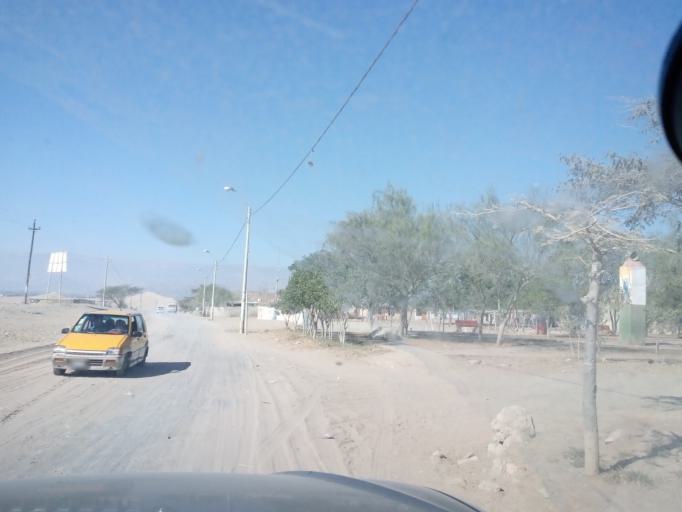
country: PE
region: Ica
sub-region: Provincia de Ica
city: Ica
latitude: -14.0797
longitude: -75.7701
